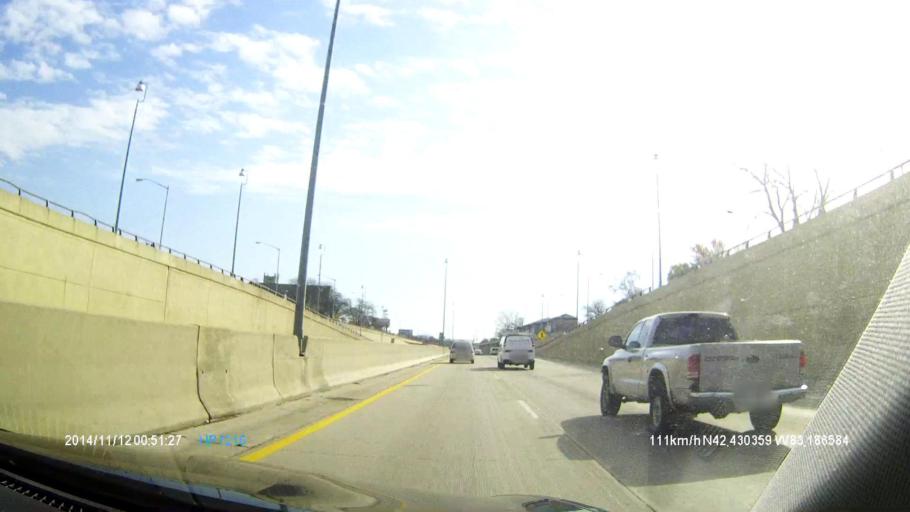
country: US
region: Michigan
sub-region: Oakland County
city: Oak Park
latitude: 42.4300
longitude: -83.1862
